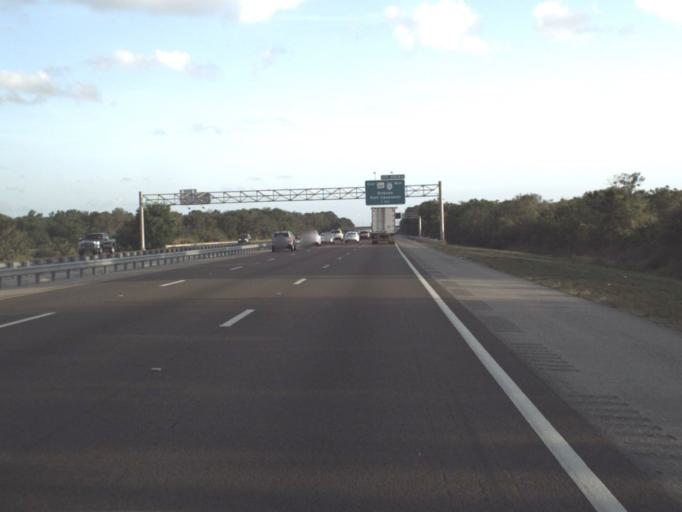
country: US
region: Florida
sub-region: Brevard County
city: Port Saint John
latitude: 28.4336
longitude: -80.8205
